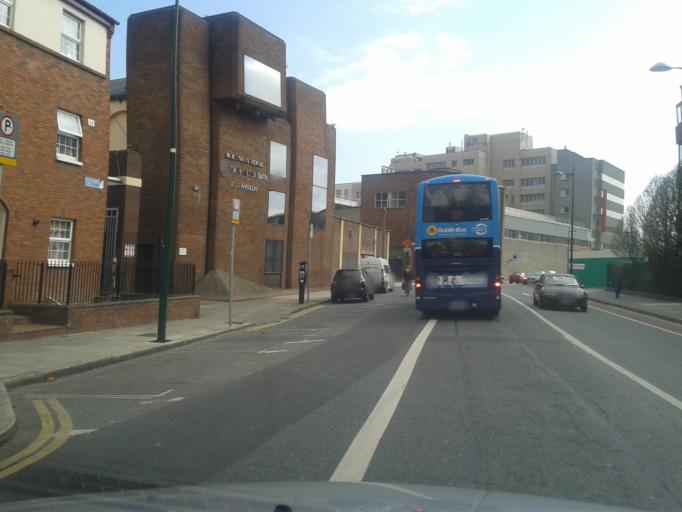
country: IE
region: Leinster
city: Rathmines
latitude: 53.3398
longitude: -6.2697
